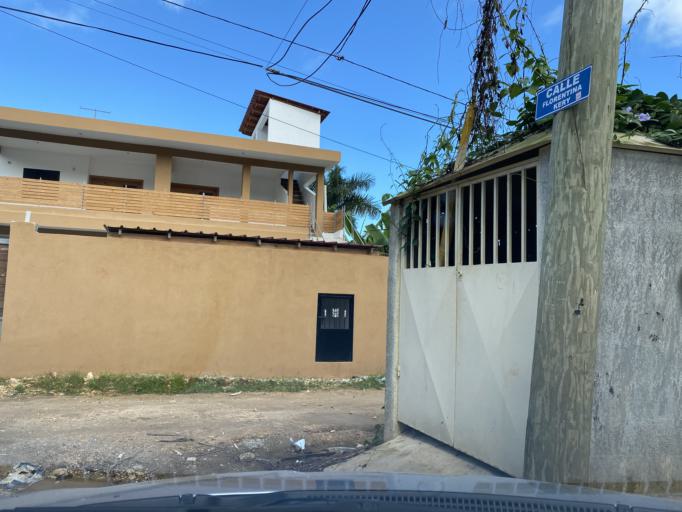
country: DO
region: Samana
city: Las Terrenas
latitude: 19.3039
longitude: -69.5410
